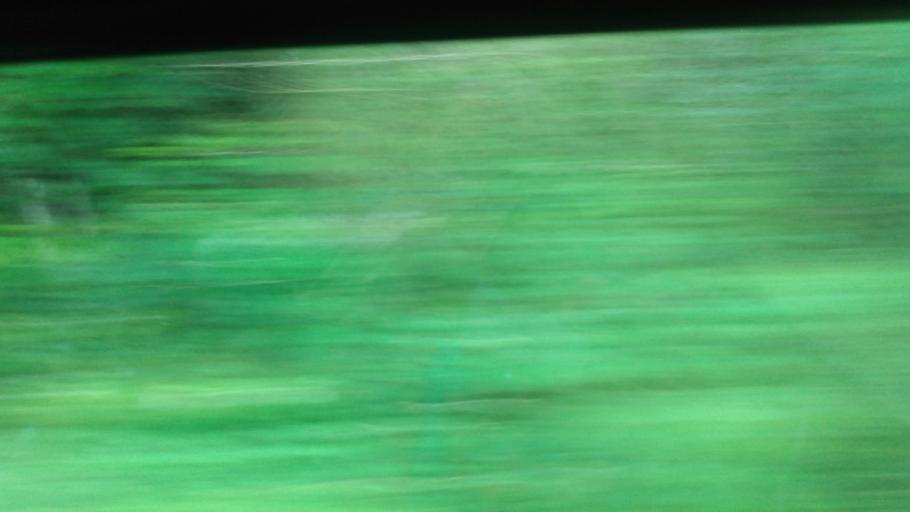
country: BR
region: Pernambuco
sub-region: Quipapa
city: Quipapa
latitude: -8.7878
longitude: -35.9672
